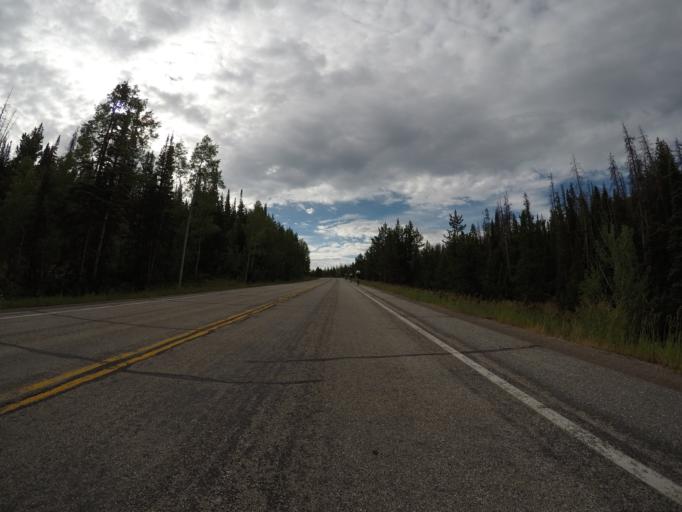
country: US
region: Wyoming
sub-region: Carbon County
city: Saratoga
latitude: 41.3332
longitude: -106.5184
